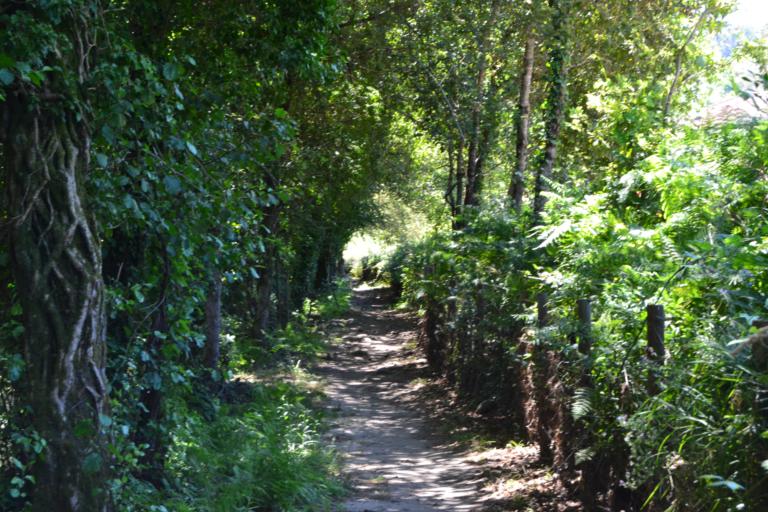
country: PT
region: Viana do Castelo
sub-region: Arcos de Valdevez
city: Mozelos
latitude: 41.9009
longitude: -8.4404
